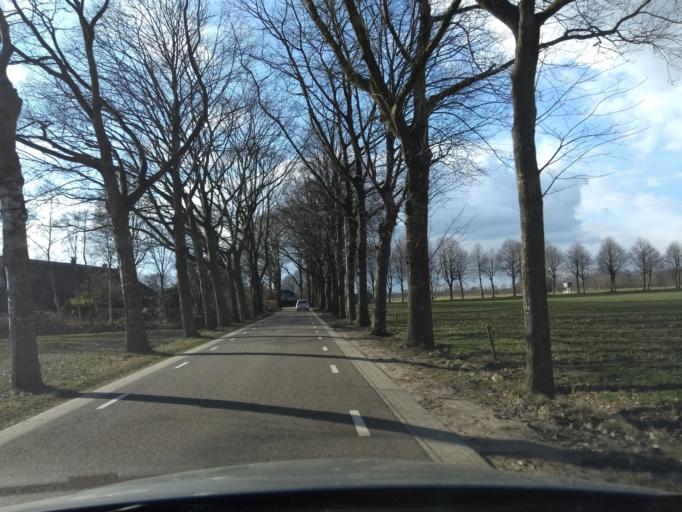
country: NL
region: Drenthe
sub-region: Gemeente Meppel
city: Meppel
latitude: 52.7063
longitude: 6.2554
